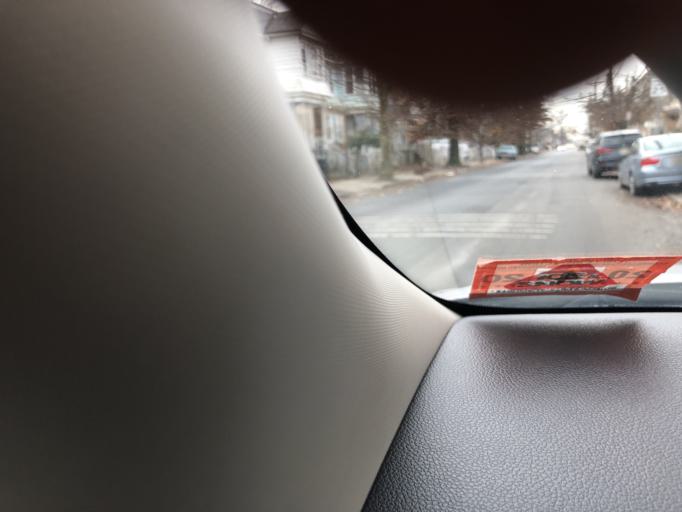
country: US
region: New Jersey
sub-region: Essex County
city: Irvington
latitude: 40.7196
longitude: -74.2188
